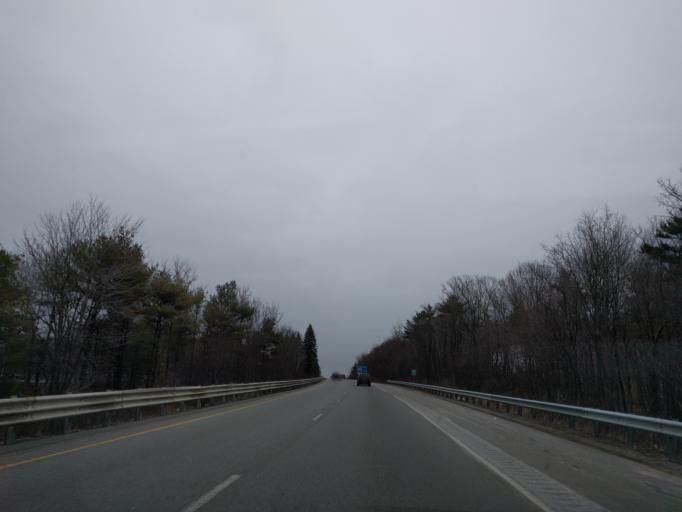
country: US
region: Massachusetts
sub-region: Worcester County
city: Gardner
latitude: 42.5618
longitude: -71.9706
